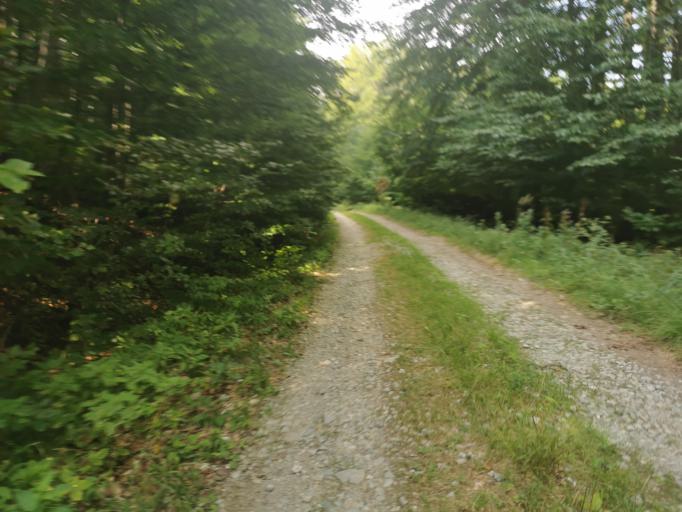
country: SK
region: Trenciansky
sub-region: Okres Myjava
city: Myjava
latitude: 48.8280
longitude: 17.5988
